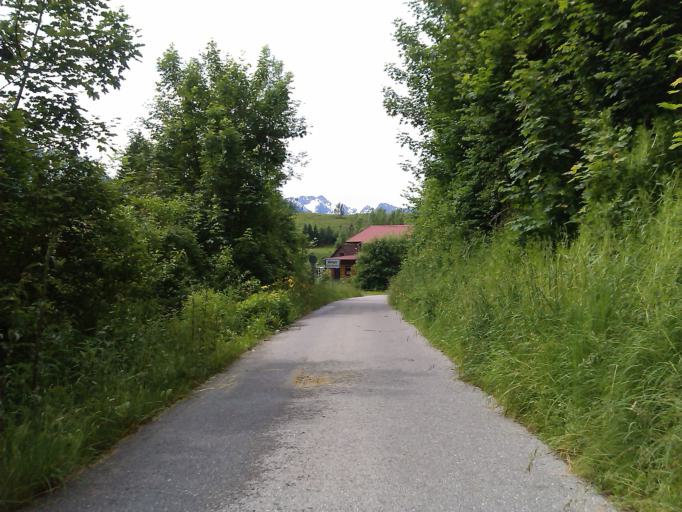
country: AT
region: Tyrol
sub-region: Politischer Bezirk Reutte
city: Lechaschau
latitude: 47.5032
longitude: 10.7059
